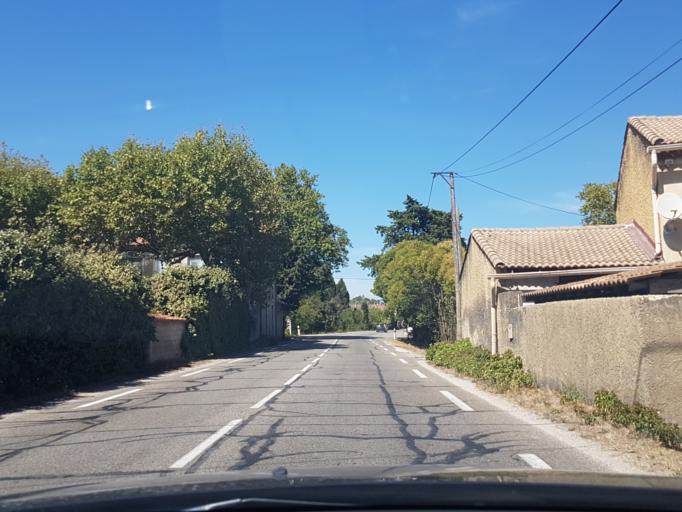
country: FR
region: Provence-Alpes-Cote d'Azur
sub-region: Departement des Bouches-du-Rhone
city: Chateaurenard
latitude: 43.8802
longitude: 4.8327
